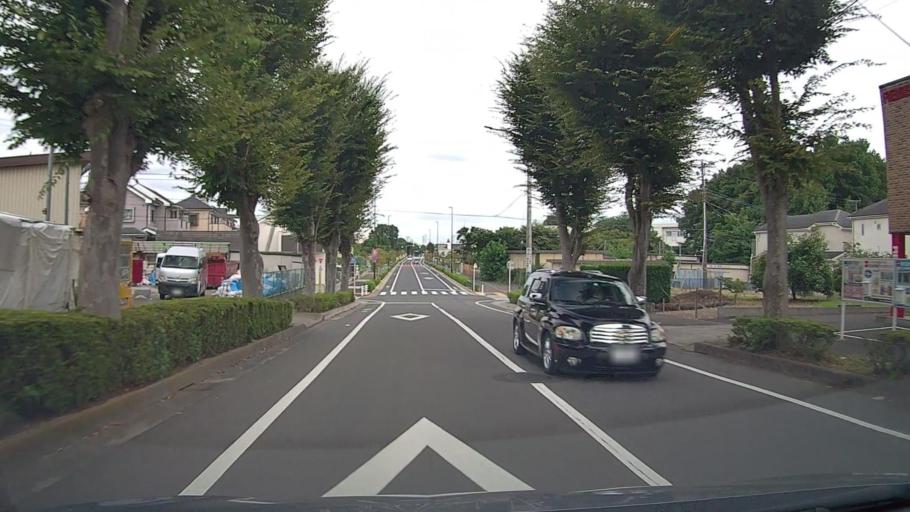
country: JP
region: Tokyo
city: Higashimurayama-shi
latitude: 35.7518
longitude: 139.4918
